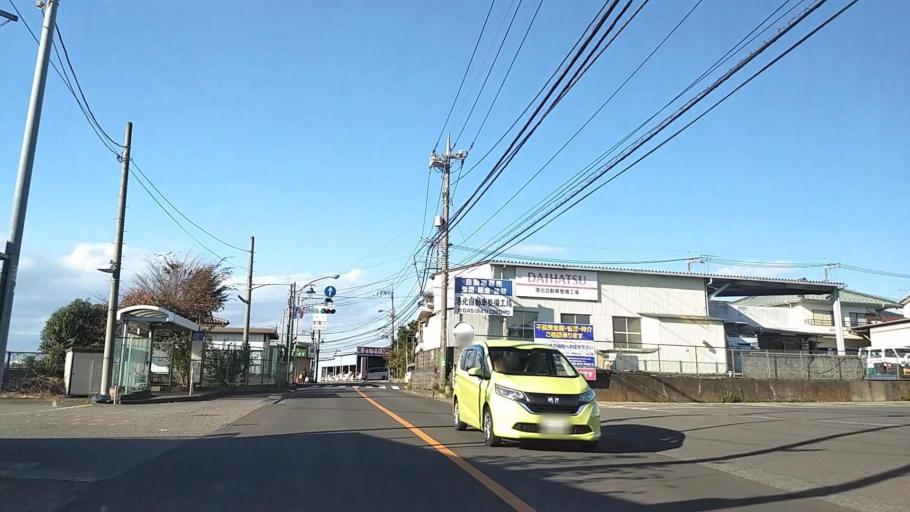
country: JP
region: Tokyo
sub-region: Machida-shi
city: Machida
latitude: 35.5342
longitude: 139.5460
